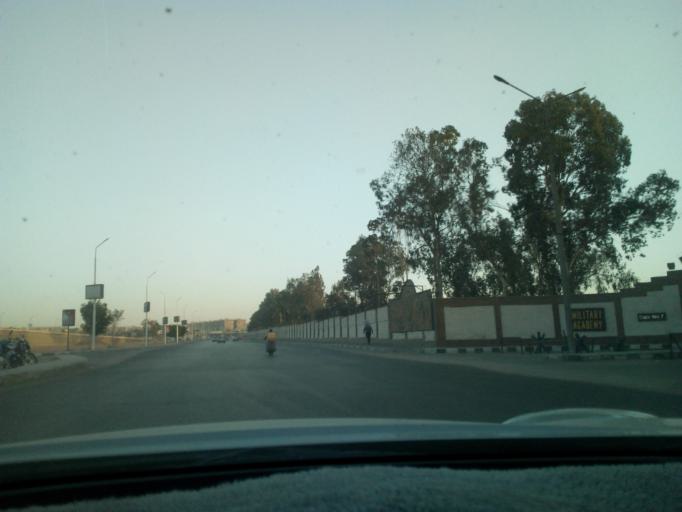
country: EG
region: Muhafazat al Qalyubiyah
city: Al Khankah
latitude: 30.1158
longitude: 31.3650
